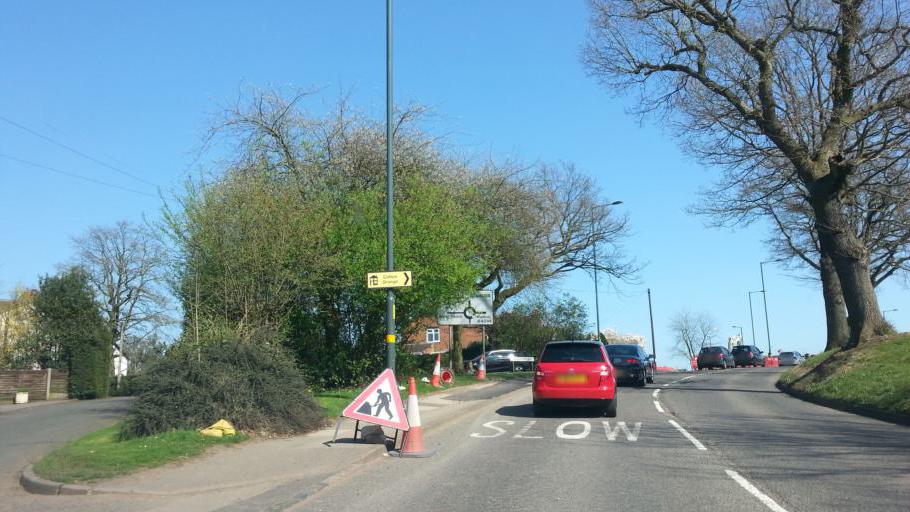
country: GB
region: England
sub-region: Worcestershire
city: Alvechurch
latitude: 52.3939
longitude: -1.9691
